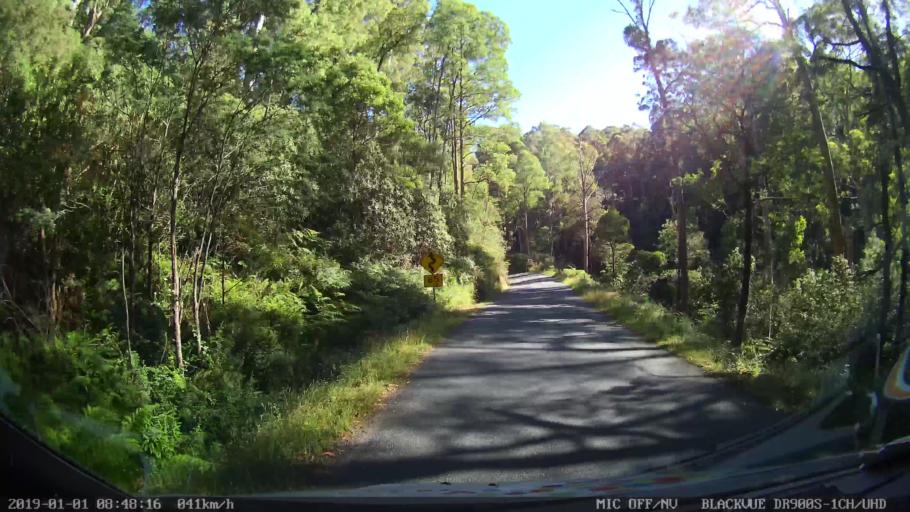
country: AU
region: New South Wales
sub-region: Snowy River
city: Jindabyne
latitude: -36.2898
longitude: 148.1992
